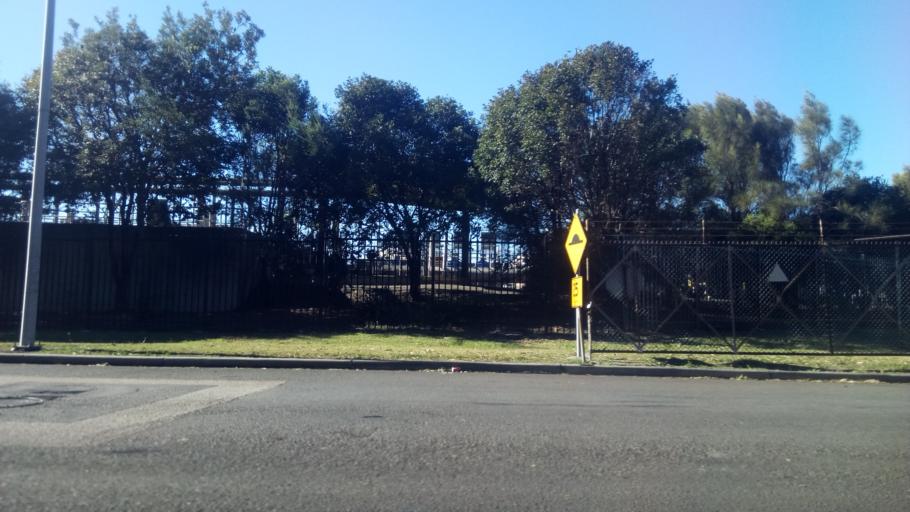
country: AU
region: New South Wales
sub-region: Wollongong
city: Coniston
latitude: -34.4422
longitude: 150.8965
